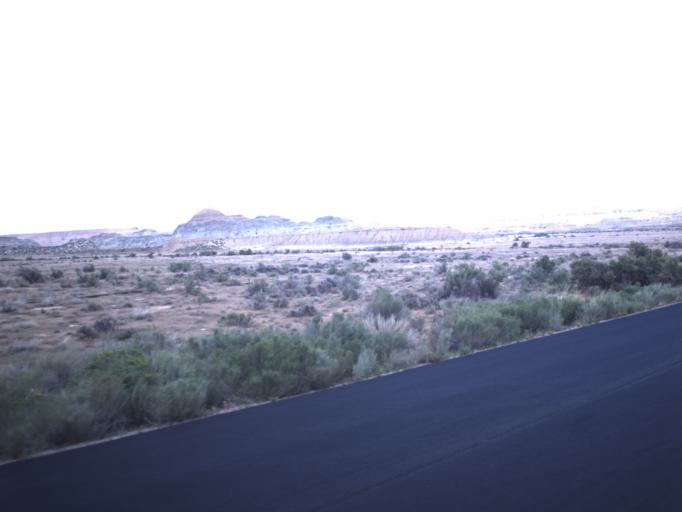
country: US
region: Utah
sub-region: Uintah County
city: Naples
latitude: 40.1153
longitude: -109.2434
